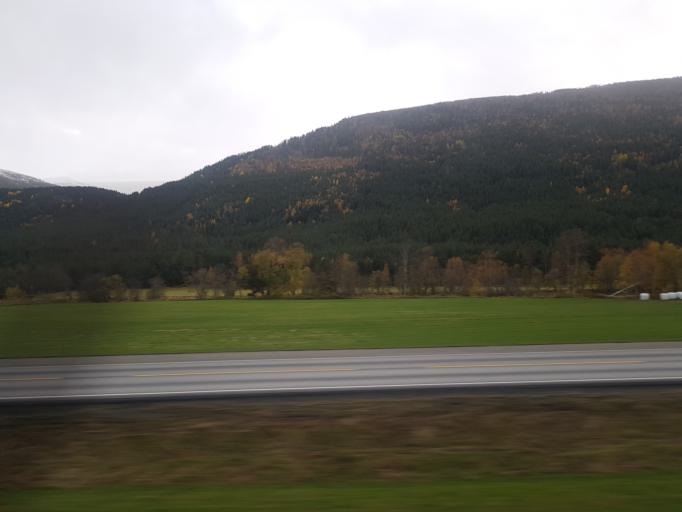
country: NO
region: Oppland
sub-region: Dovre
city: Dovre
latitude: 61.9818
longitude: 9.2458
